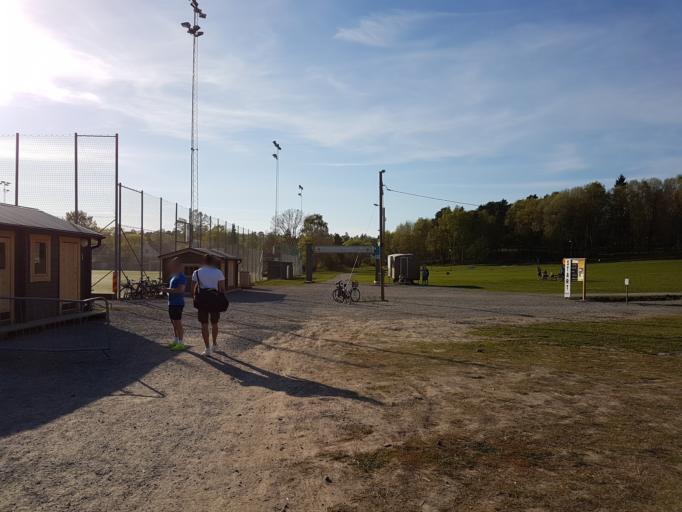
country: SE
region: Stockholm
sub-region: Solna Kommun
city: Rasunda
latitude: 59.3817
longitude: 17.9701
